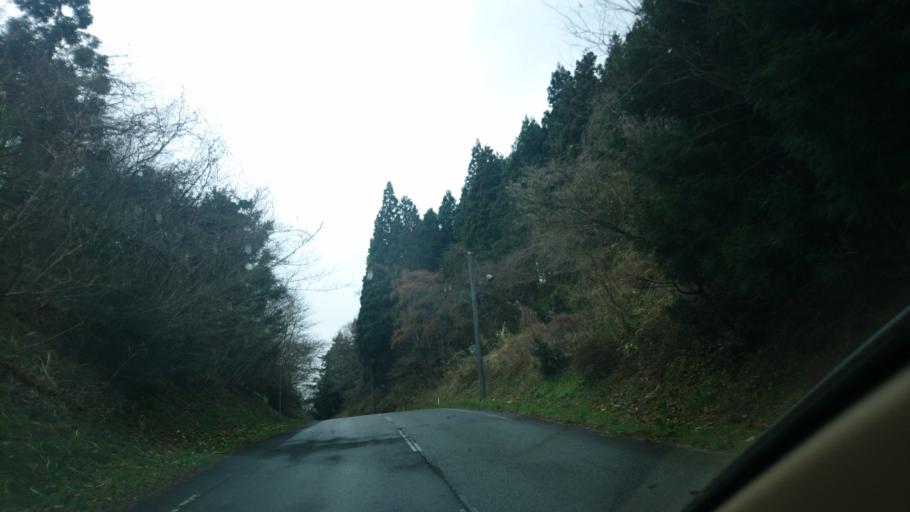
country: JP
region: Iwate
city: Ichinoseki
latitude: 38.9534
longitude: 141.3192
